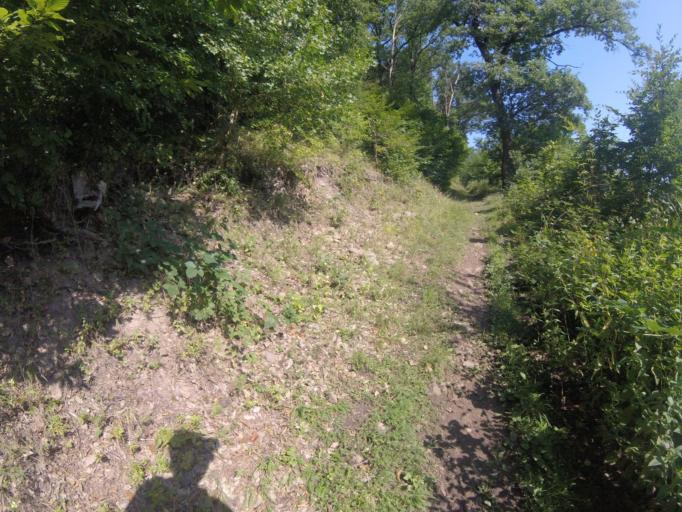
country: SK
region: Nitriansky
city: Sahy
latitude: 47.9851
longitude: 18.8956
